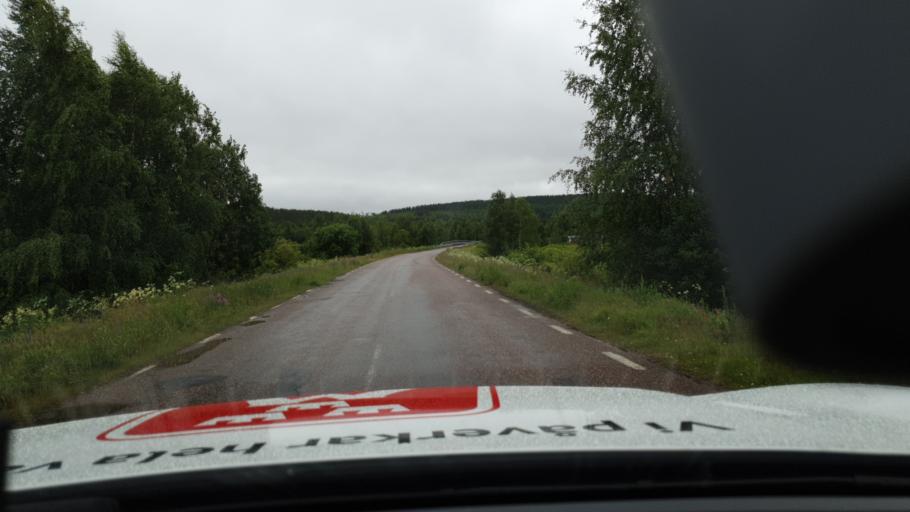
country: SE
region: Norrbotten
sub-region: Overtornea Kommun
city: OEvertornea
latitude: 66.4203
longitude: 23.6143
